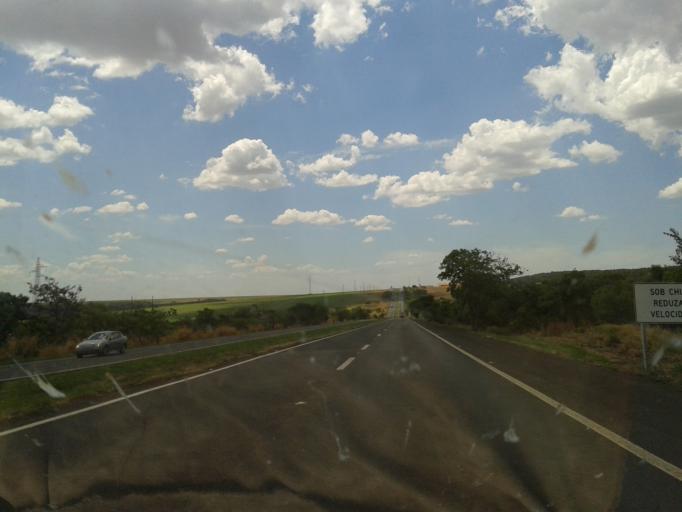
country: BR
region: Minas Gerais
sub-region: Uberlandia
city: Uberlandia
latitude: -19.0966
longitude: -48.1824
